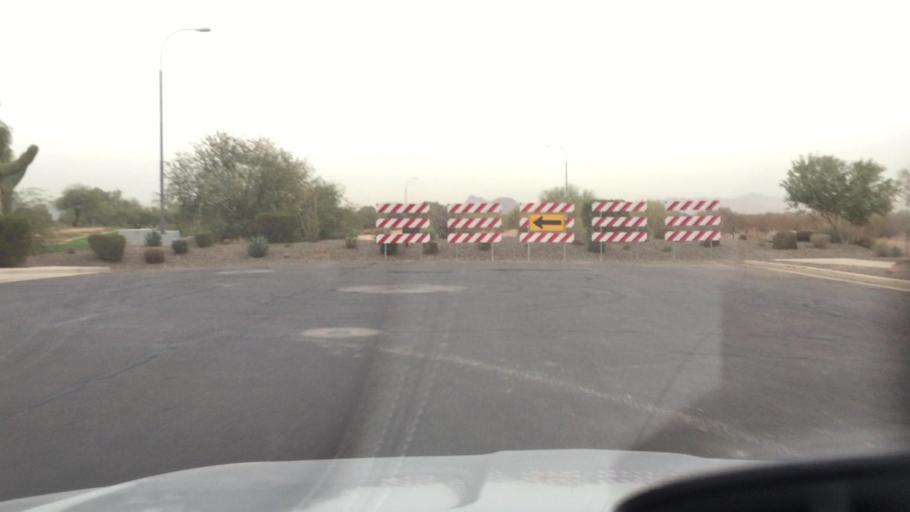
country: US
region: Arizona
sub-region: Maricopa County
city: Scottsdale
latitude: 33.5385
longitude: -111.8655
